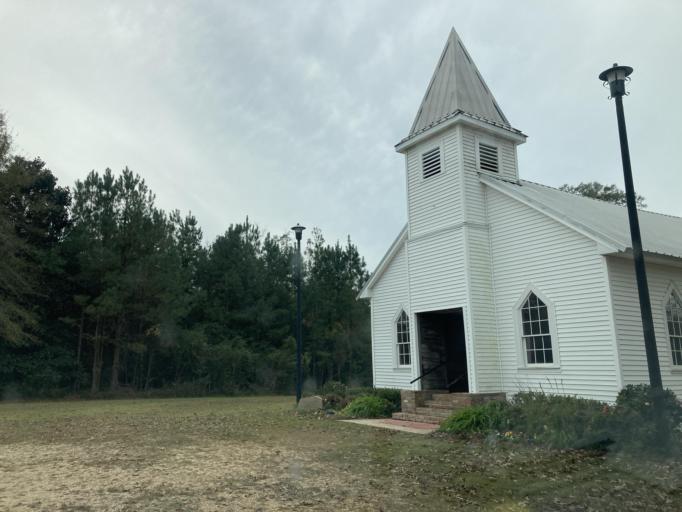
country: US
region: Mississippi
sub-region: Lamar County
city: Purvis
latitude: 31.0757
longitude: -89.4294
